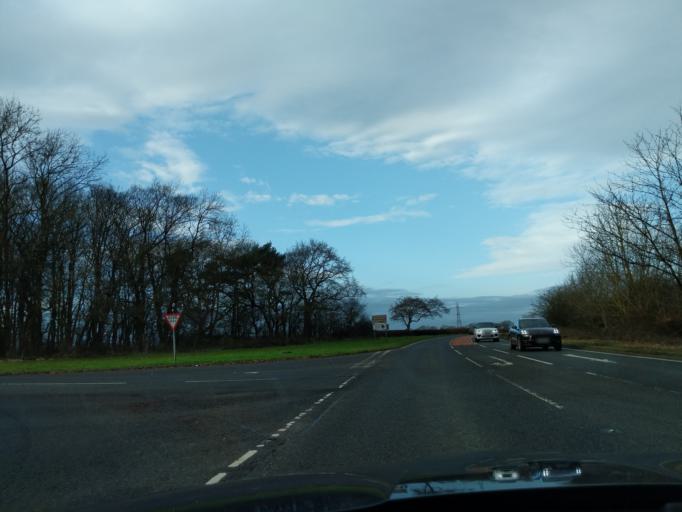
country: GB
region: England
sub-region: Northumberland
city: Ponteland
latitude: 55.0550
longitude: -1.7634
